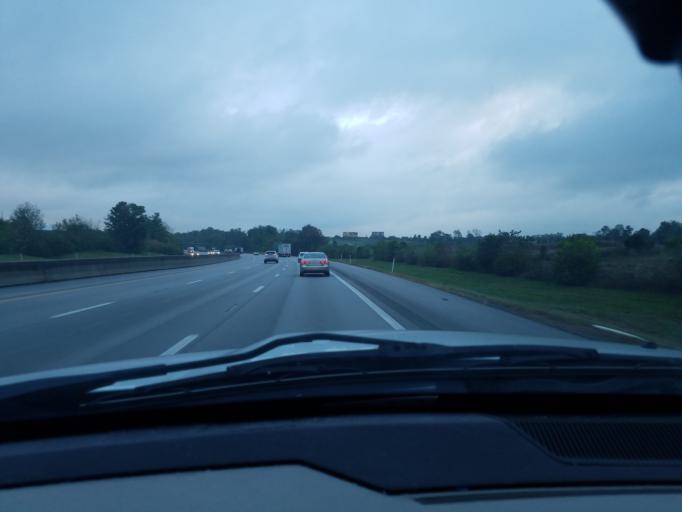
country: US
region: Kentucky
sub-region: Scott County
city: Georgetown
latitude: 38.1880
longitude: -84.5259
